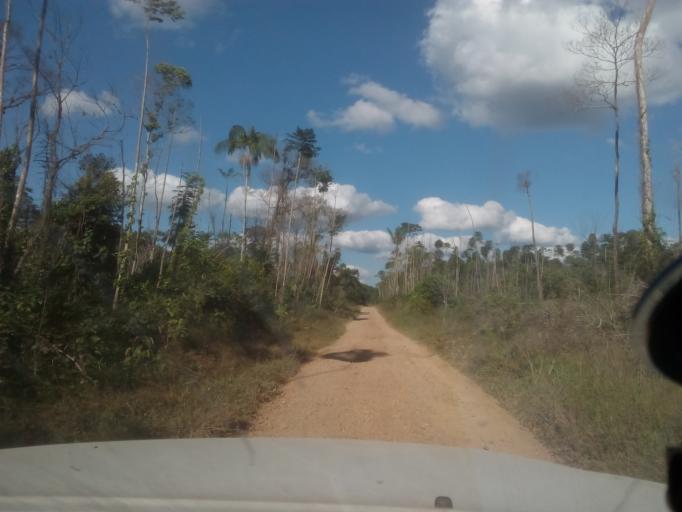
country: PE
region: Cusco
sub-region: Provincia de Quispicanchis
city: Quince Mil
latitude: -12.6441
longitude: -70.3639
